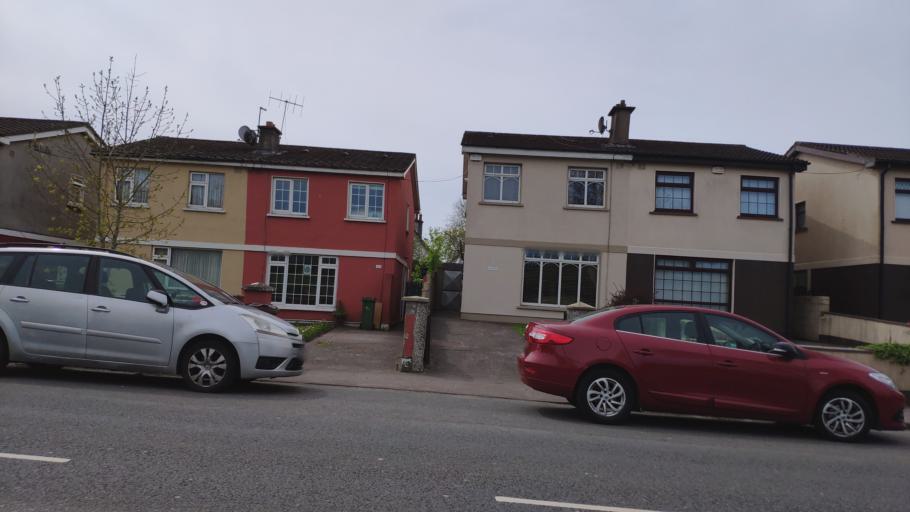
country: IE
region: Munster
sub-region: County Cork
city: Cork
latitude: 51.9185
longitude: -8.4499
